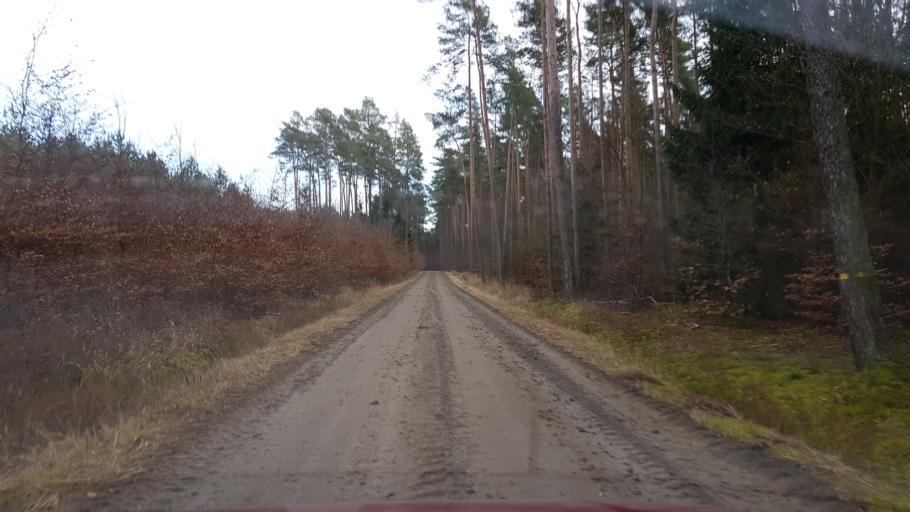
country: PL
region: Lubusz
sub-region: Powiat strzelecko-drezdenecki
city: Strzelce Krajenskie
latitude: 52.9085
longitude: 15.3961
